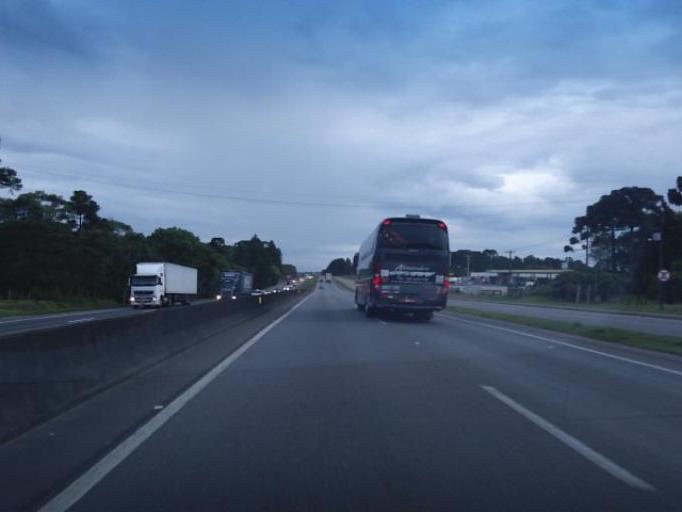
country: BR
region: Parana
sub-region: Sao Jose Dos Pinhais
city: Sao Jose dos Pinhais
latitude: -25.6492
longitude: -49.1580
